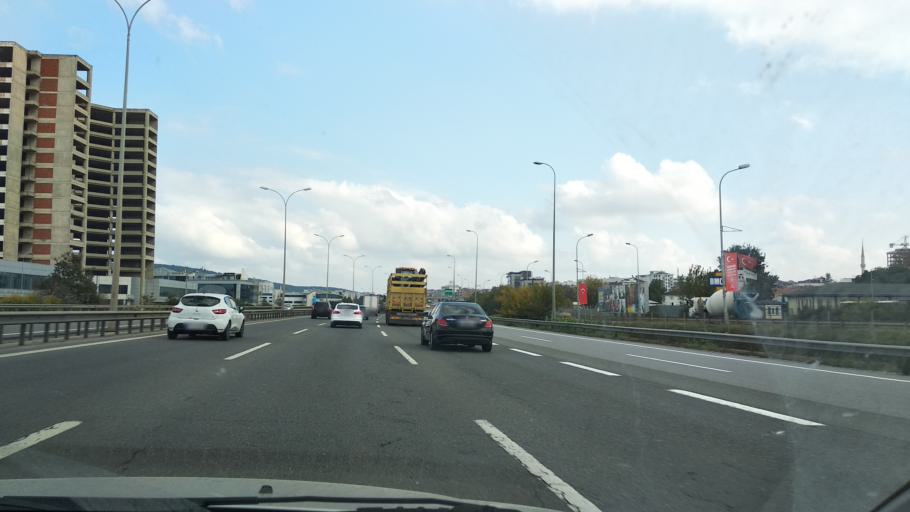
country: TR
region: Istanbul
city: Sultanbeyli
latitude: 40.9752
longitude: 29.2472
